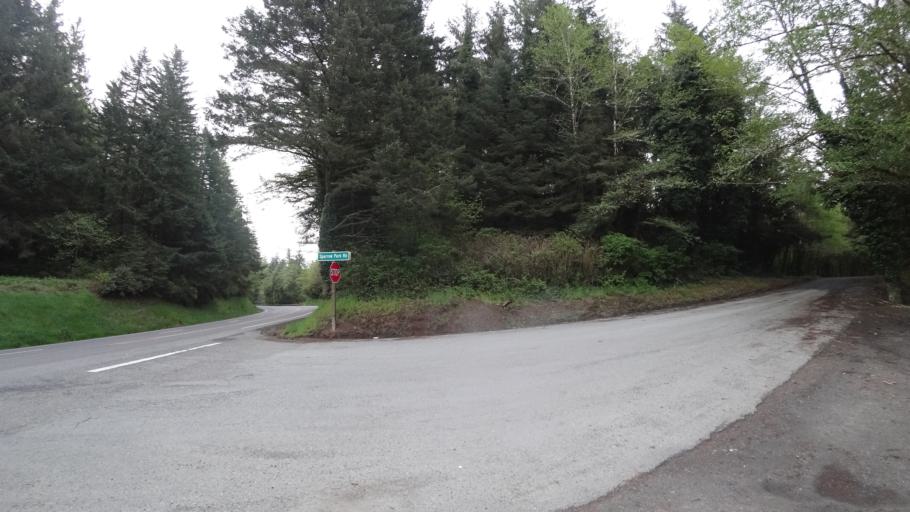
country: US
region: Oregon
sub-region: Douglas County
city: Reedsport
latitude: 43.7528
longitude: -124.1266
